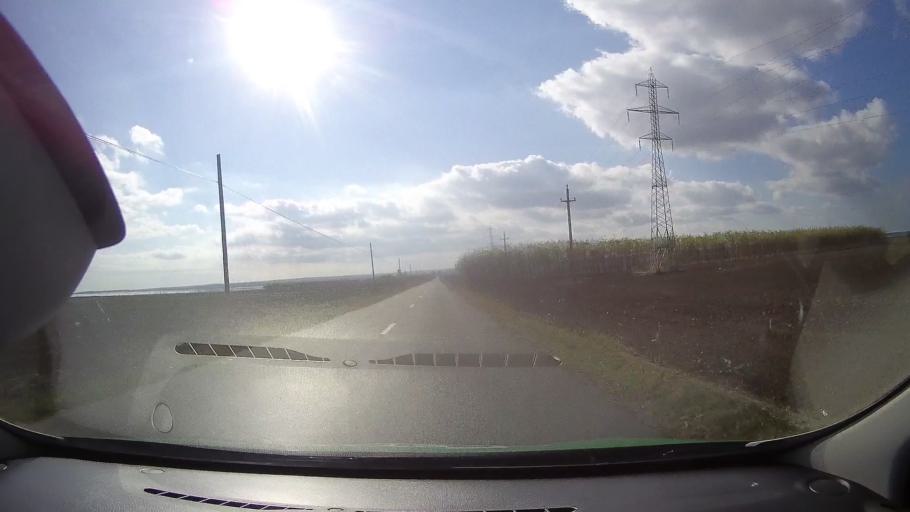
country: RO
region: Constanta
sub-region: Comuna Istria
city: Istria
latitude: 44.5527
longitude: 28.6963
